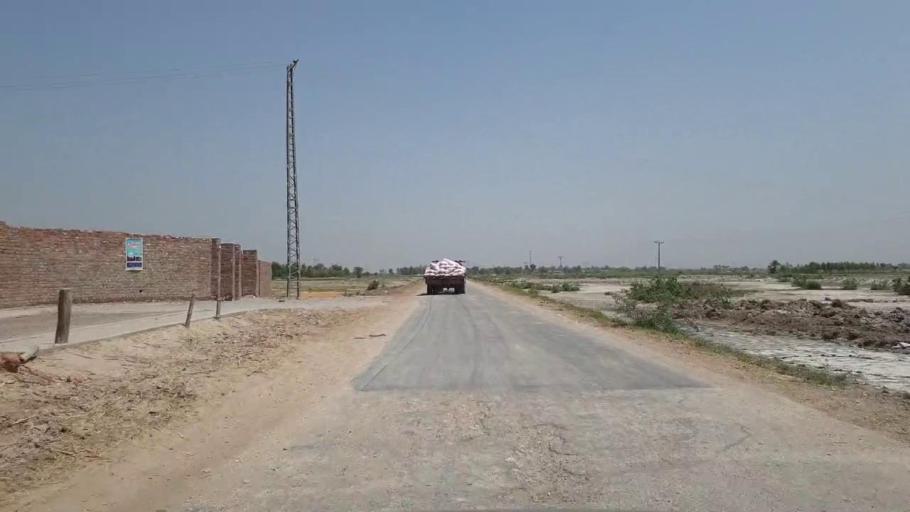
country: PK
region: Sindh
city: Adilpur
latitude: 27.8805
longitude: 69.2868
